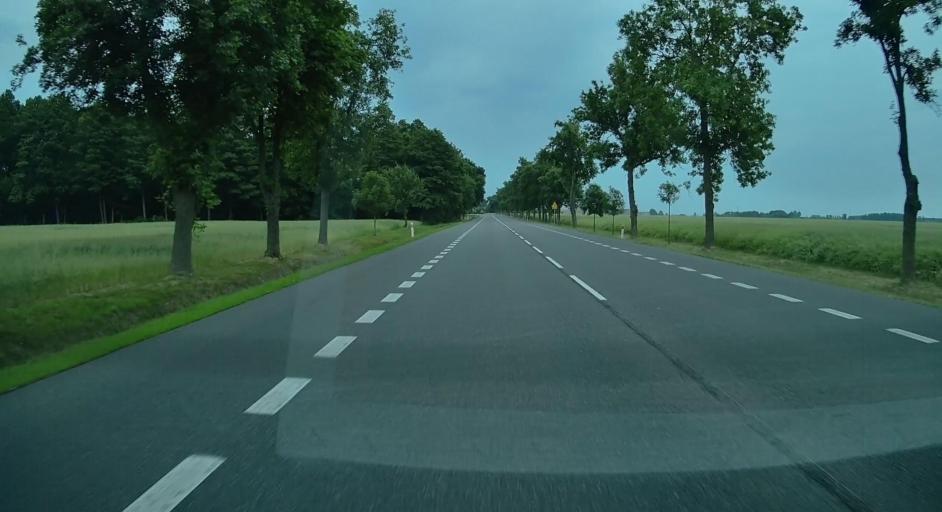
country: PL
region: Lublin Voivodeship
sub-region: Powiat lukowski
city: Trzebieszow
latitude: 52.0647
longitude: 22.5423
